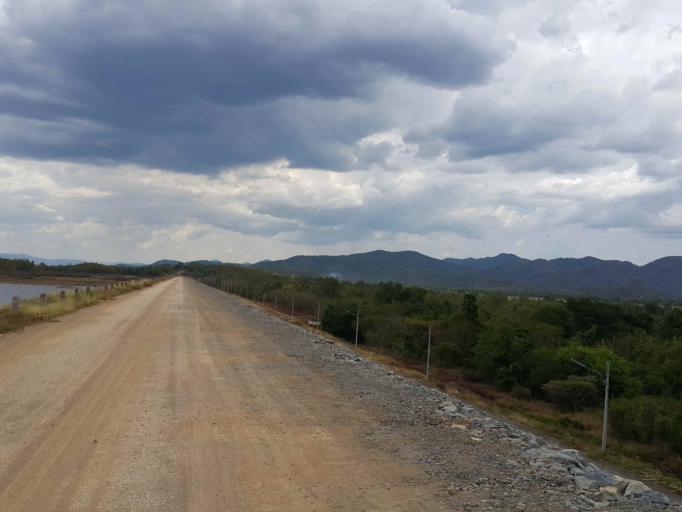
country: TH
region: Sukhothai
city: Thung Saliam
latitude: 17.3130
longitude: 99.4252
